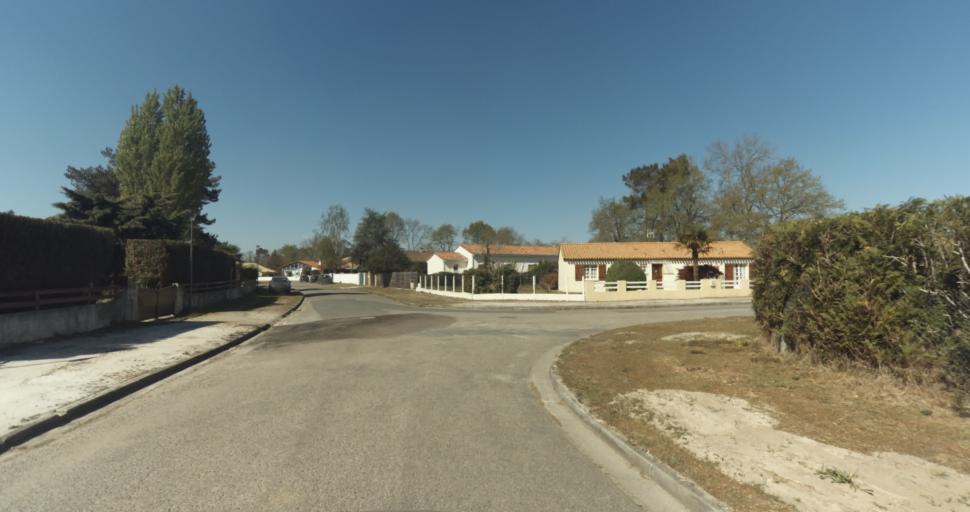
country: FR
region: Aquitaine
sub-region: Departement de la Gironde
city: Martignas-sur-Jalle
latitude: 44.7996
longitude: -0.7879
